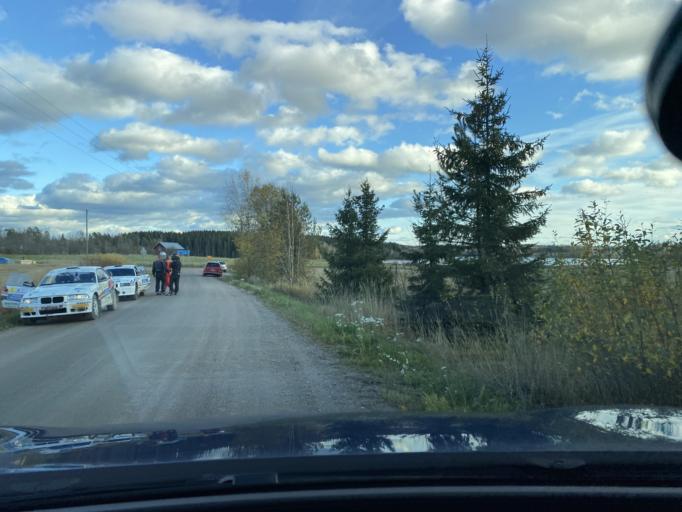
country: FI
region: Uusimaa
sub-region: Porvoo
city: Pukkila
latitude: 60.7490
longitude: 25.5648
